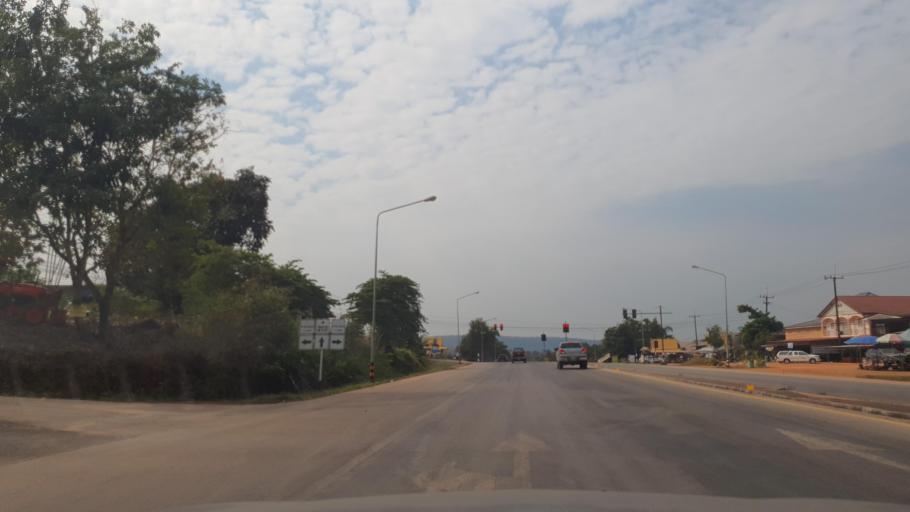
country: TH
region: Changwat Bueng Kan
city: Bung Khla
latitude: 18.2763
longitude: 103.8569
